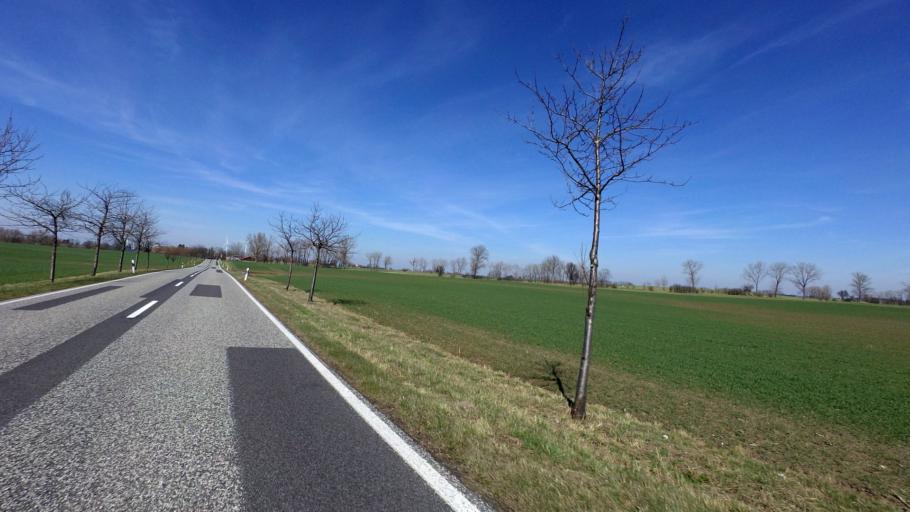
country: DE
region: Brandenburg
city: Furstenwalde
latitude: 52.4229
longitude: 14.0463
